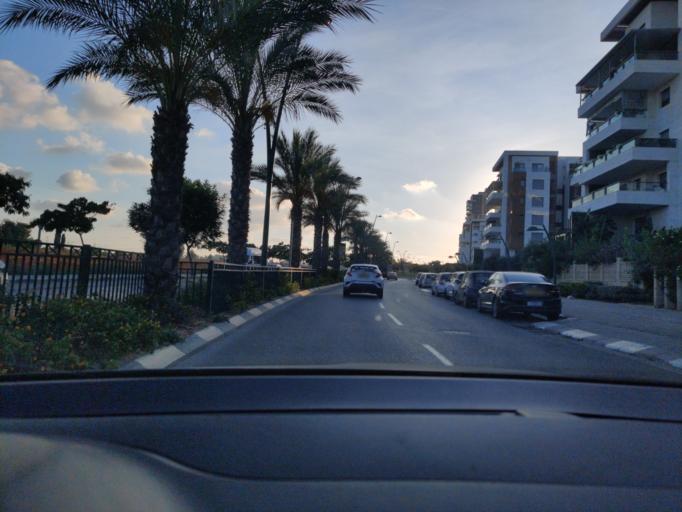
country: IL
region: Central District
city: Elyakhin
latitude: 32.4268
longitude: 34.9403
